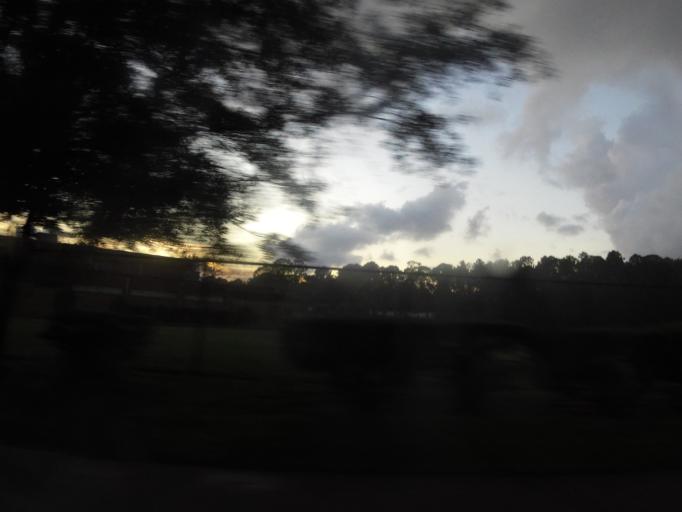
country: US
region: Florida
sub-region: Duval County
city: Jacksonville
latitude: 30.2487
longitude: -81.6225
